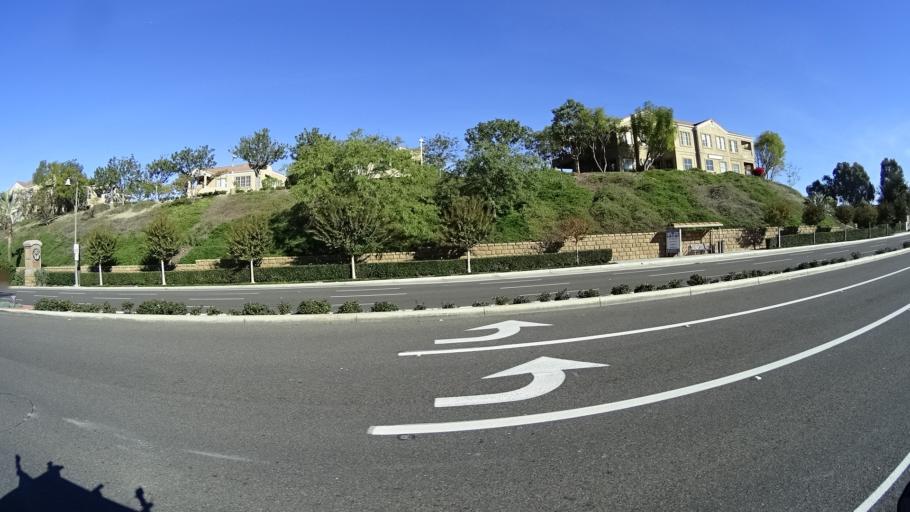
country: US
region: California
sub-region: Orange County
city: Ladera Ranch
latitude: 33.5636
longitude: -117.6592
